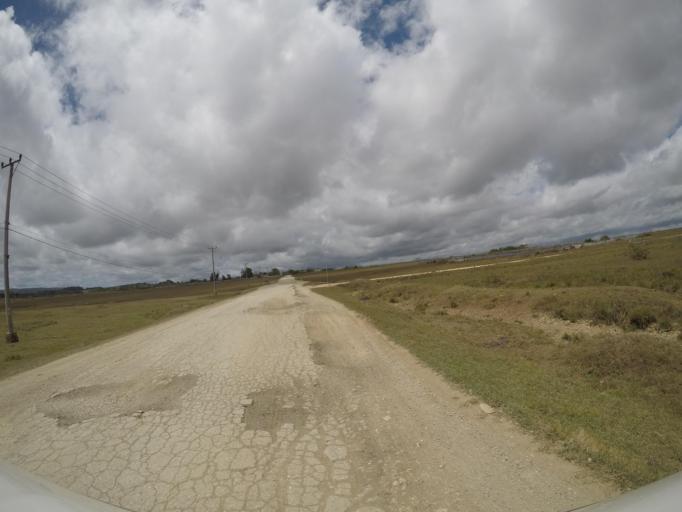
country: TL
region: Lautem
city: Lospalos
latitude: -8.4411
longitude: 126.9897
